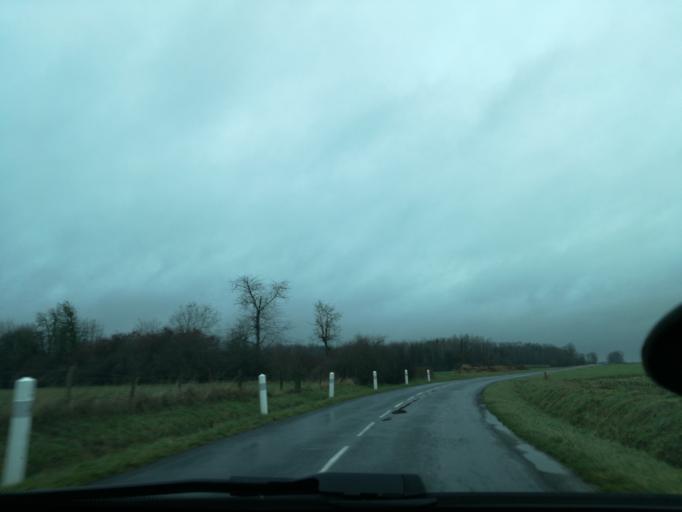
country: FR
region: Lorraine
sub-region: Departement de la Meuse
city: Clermont-en-Argonne
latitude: 48.9879
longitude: 5.0709
